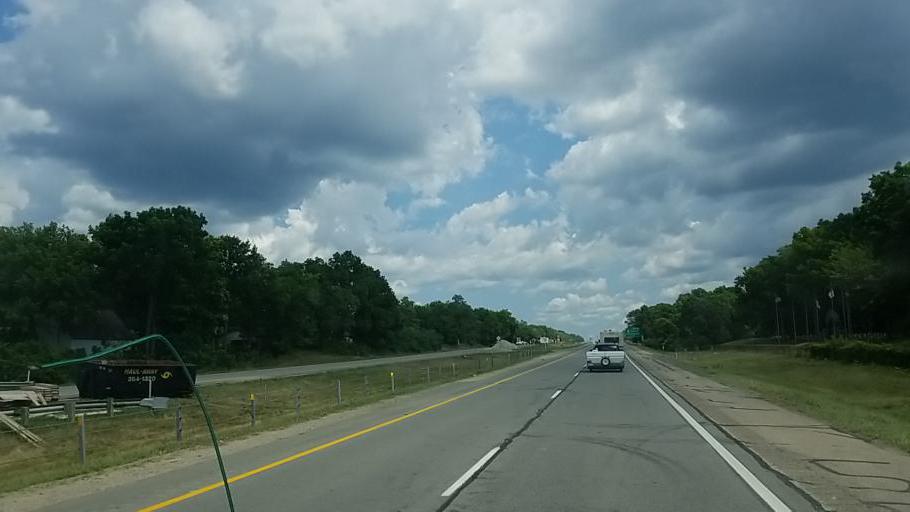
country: US
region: Michigan
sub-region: Kent County
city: Comstock Park
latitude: 43.0210
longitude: -85.6593
